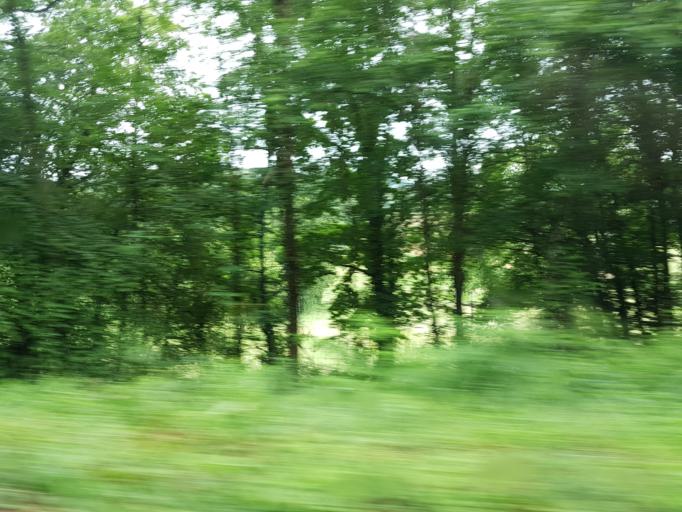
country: FR
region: Bourgogne
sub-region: Departement de la Nievre
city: Chateau-Chinon(Ville)
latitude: 47.1570
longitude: 3.8639
